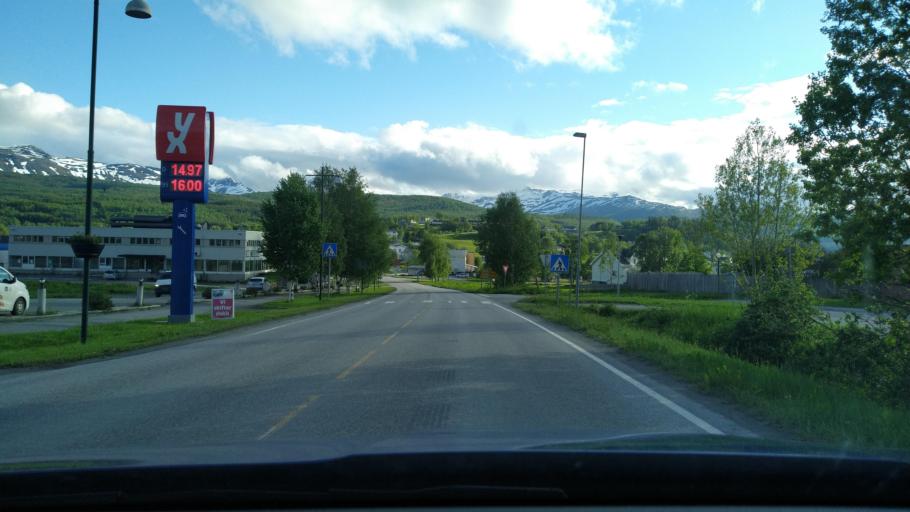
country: NO
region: Troms
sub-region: Sorreisa
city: Sorreisa
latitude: 69.1467
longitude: 18.1572
